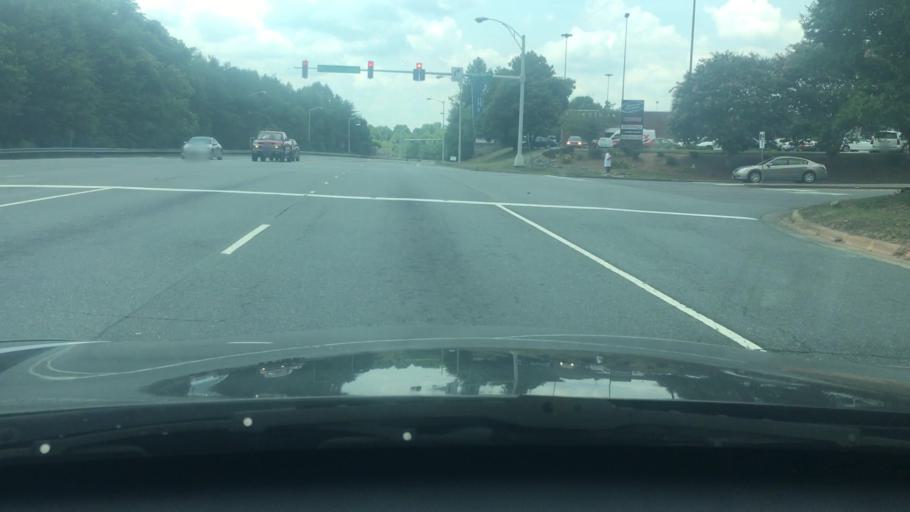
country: US
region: North Carolina
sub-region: Forsyth County
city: Winston-Salem
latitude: 36.0702
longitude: -80.2972
